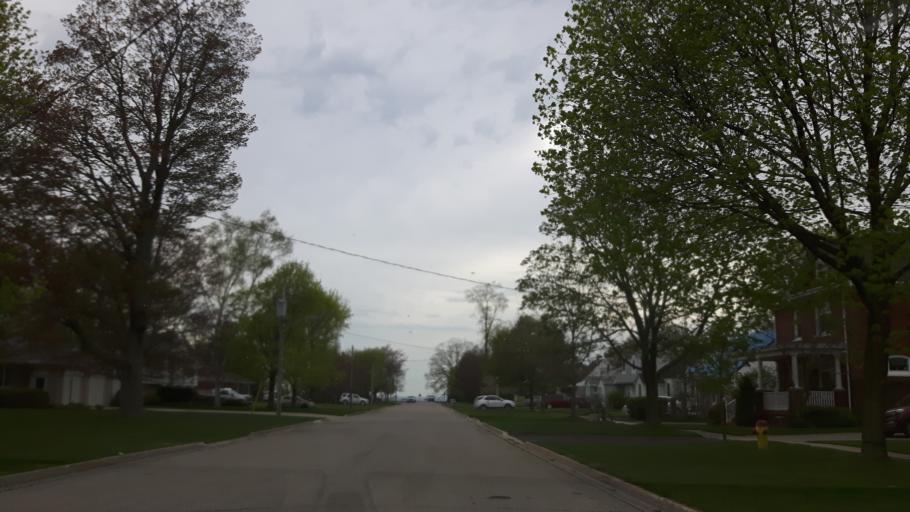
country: CA
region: Ontario
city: Goderich
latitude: 43.7406
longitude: -81.7216
